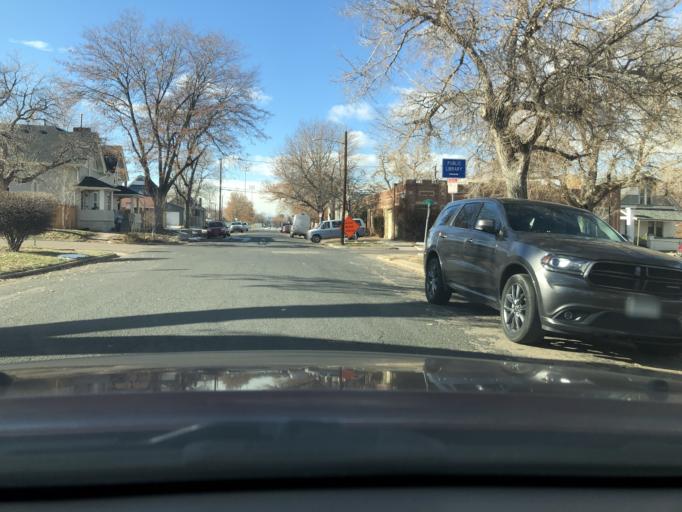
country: US
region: Colorado
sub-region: Denver County
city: Denver
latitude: 39.7557
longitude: -104.9643
